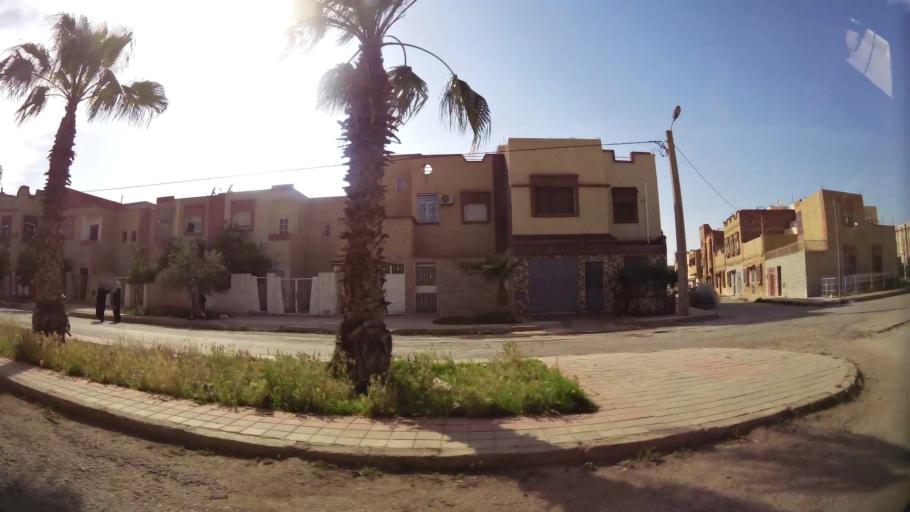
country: MA
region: Oriental
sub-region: Oujda-Angad
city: Oujda
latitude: 34.7130
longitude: -1.8825
